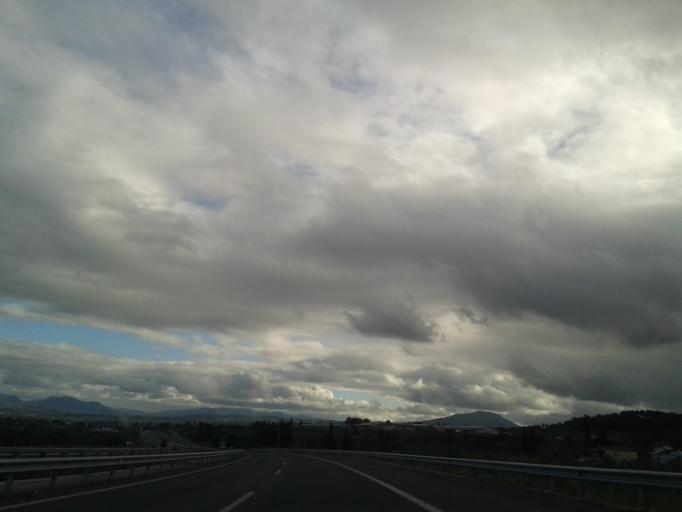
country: GR
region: Peloponnese
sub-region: Nomos Korinthias
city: Sikyon
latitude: 37.9831
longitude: 22.7356
